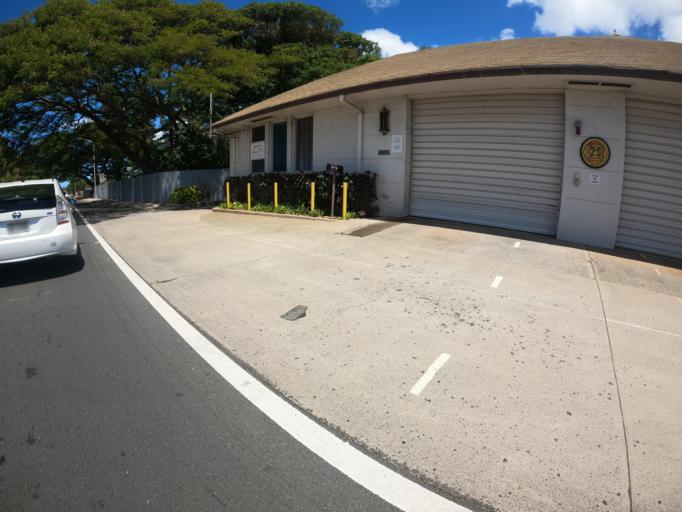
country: US
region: Hawaii
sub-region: Honolulu County
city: Waimanalo
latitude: 21.2769
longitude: -157.7598
